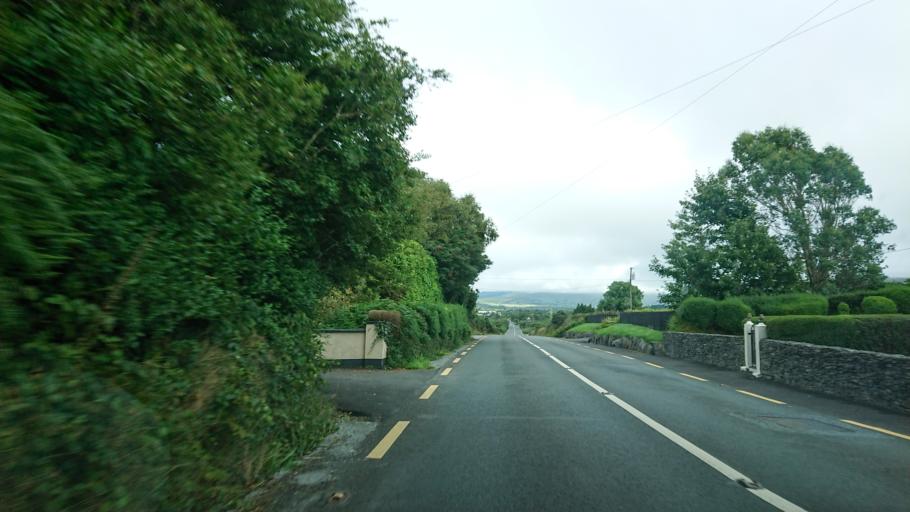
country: IE
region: Munster
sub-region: Ciarrai
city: Cahersiveen
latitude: 51.9573
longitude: -10.1916
